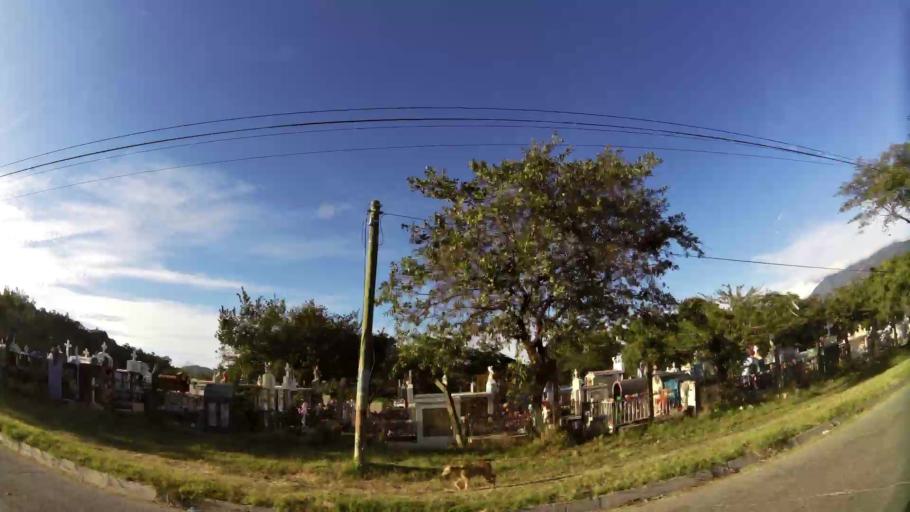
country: SV
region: Santa Ana
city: Metapan
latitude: 14.3279
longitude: -89.4547
